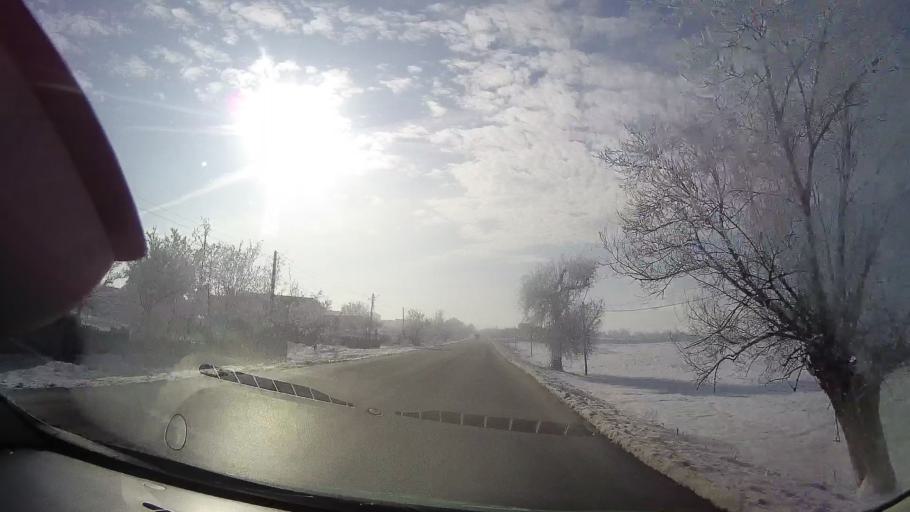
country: RO
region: Neamt
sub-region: Comuna Timisesti
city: Timisesti
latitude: 47.2393
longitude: 26.5380
